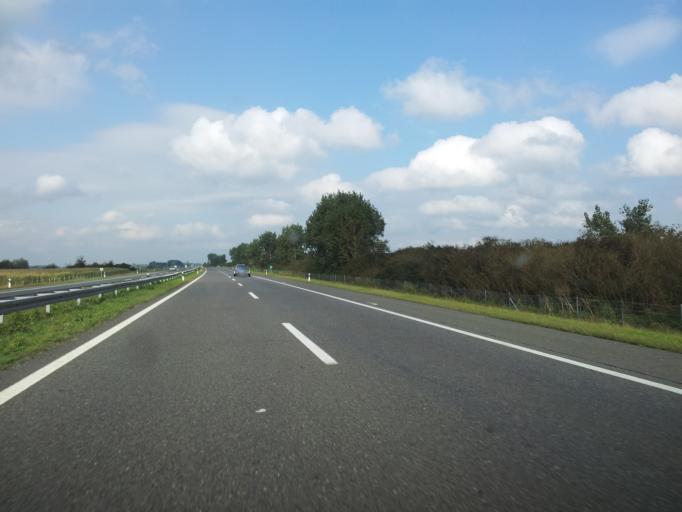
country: HR
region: Brodsko-Posavska
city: Vrbova
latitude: 45.2079
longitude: 17.5572
